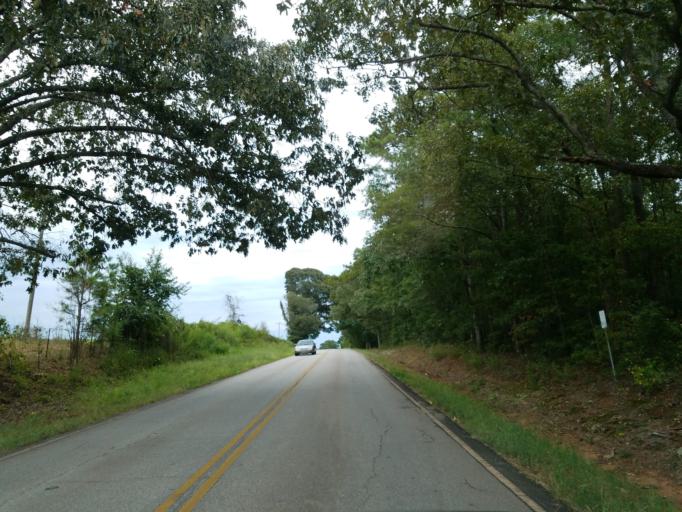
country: US
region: Georgia
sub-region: Monroe County
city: Forsyth
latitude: 32.9885
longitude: -84.0264
